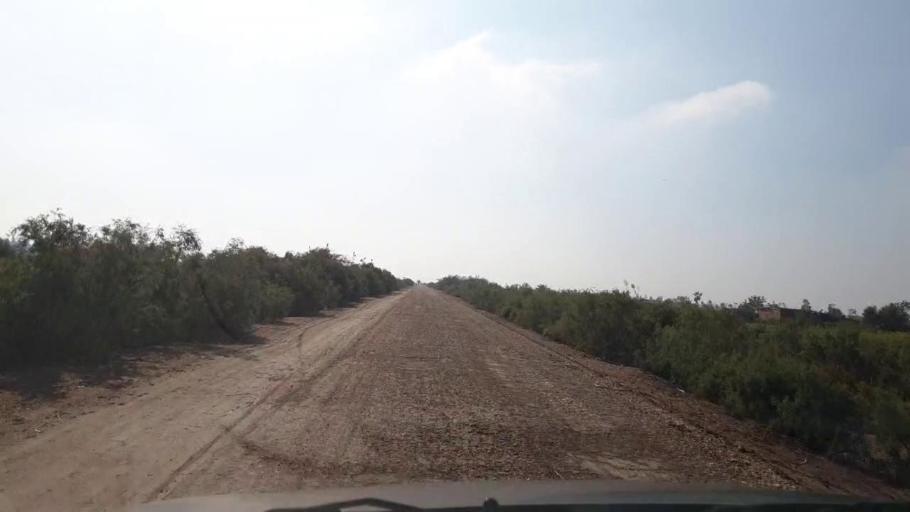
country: PK
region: Sindh
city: Sinjhoro
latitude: 26.0434
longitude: 68.7784
